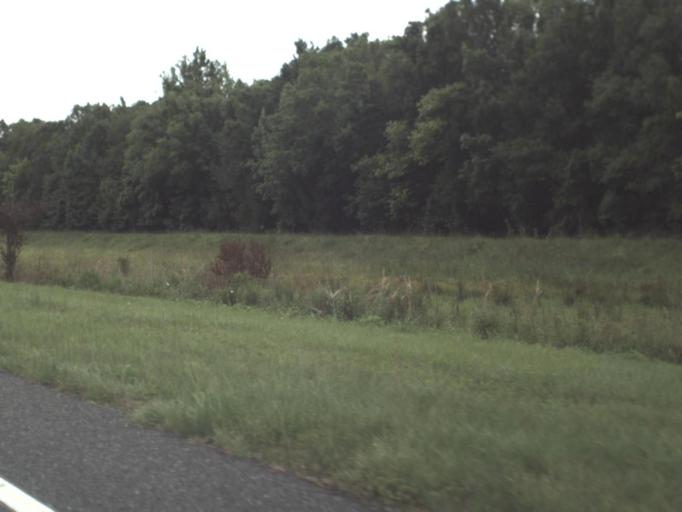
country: US
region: Florida
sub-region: Levy County
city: Williston Highlands
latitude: 29.2313
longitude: -82.7097
